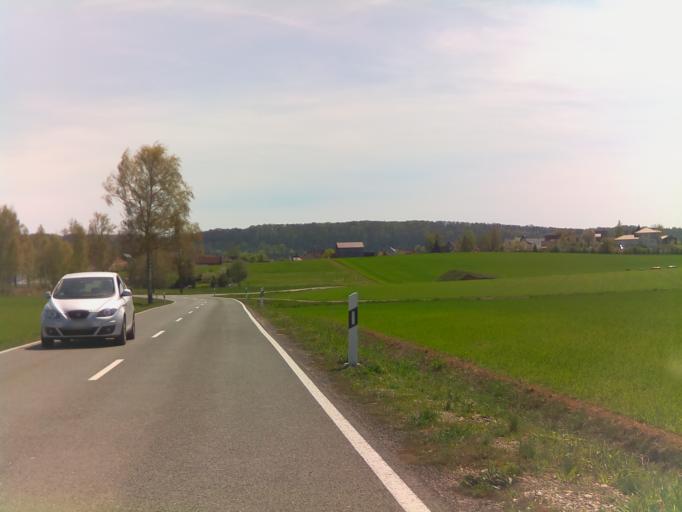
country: DE
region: Thuringia
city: Veilsdorf
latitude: 50.3141
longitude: 10.8011
